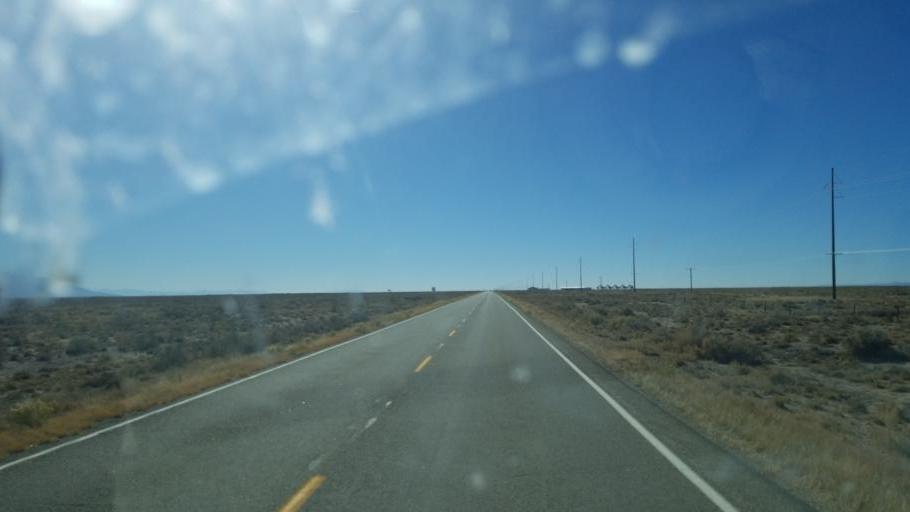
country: US
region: Colorado
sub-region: Saguache County
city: Saguache
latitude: 37.9573
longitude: -105.9039
